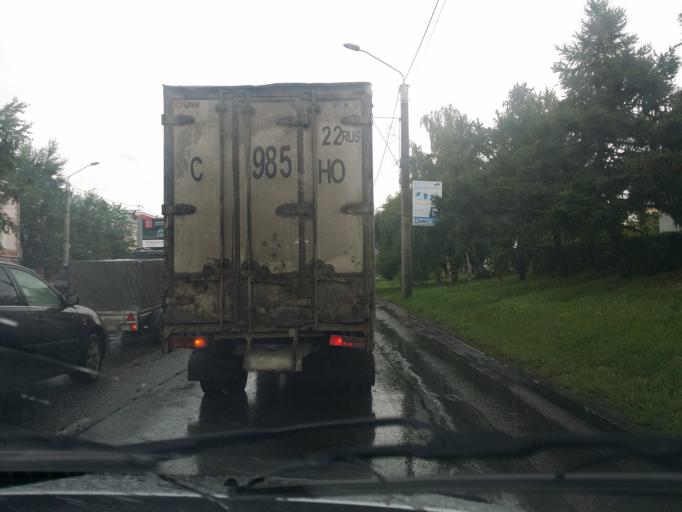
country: RU
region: Altai Krai
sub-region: Gorod Barnaulskiy
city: Barnaul
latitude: 53.3471
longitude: 83.7598
